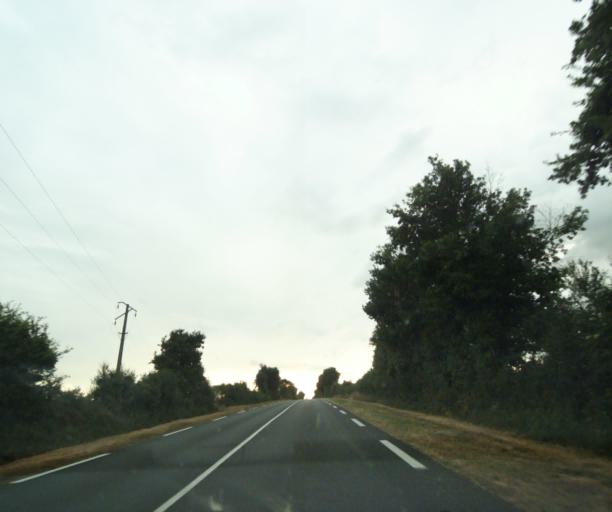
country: FR
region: Pays de la Loire
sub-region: Departement de la Vendee
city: Moutiers-les-Mauxfaits
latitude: 46.4568
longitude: -1.4315
